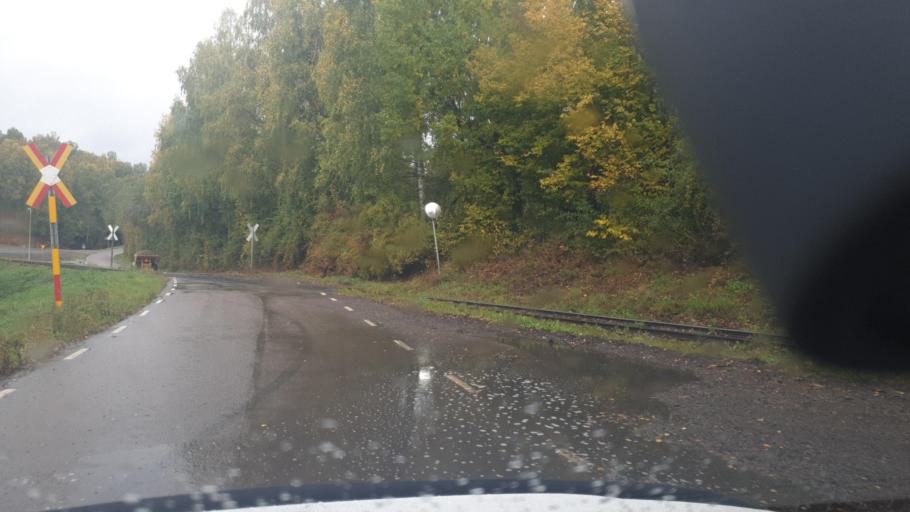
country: SE
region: Vaermland
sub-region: Sunne Kommun
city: Sunne
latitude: 59.7972
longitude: 13.1232
